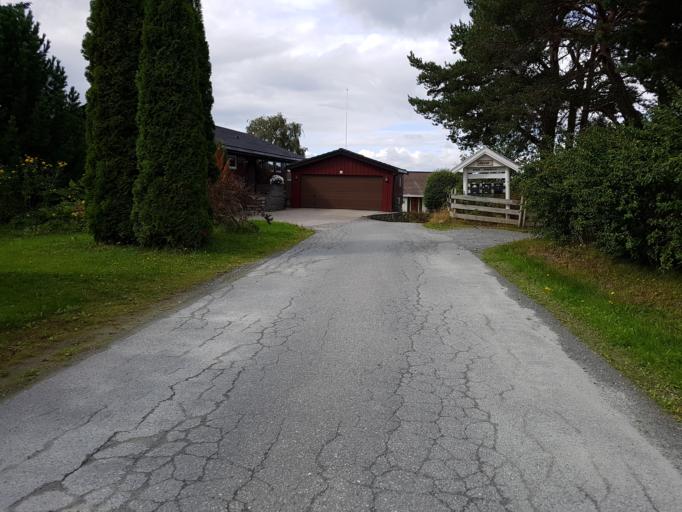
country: NO
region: Sor-Trondelag
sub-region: Trondheim
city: Trondheim
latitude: 63.4179
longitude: 10.4676
